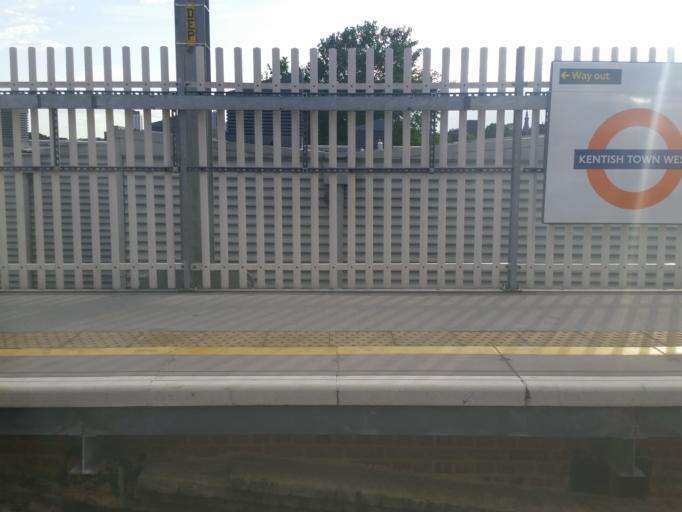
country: GB
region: England
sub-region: Greater London
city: Camden Town
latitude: 51.5473
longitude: -0.1469
